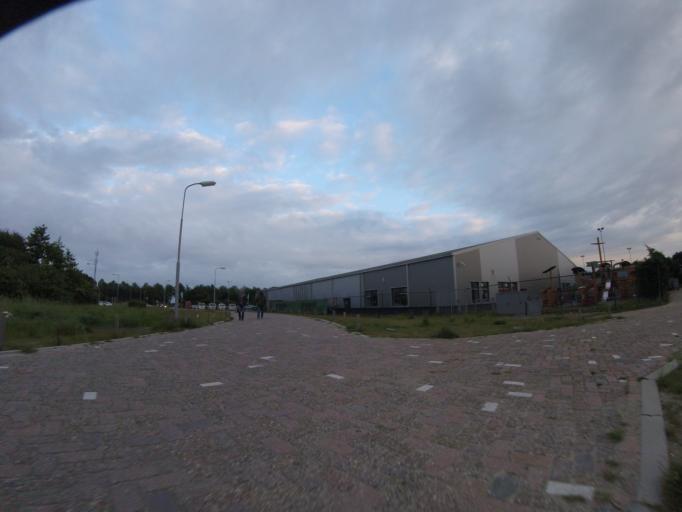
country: NL
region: North Holland
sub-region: Gemeente Haarlemmermeer
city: Hoofddorp
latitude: 52.2908
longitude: 4.6655
